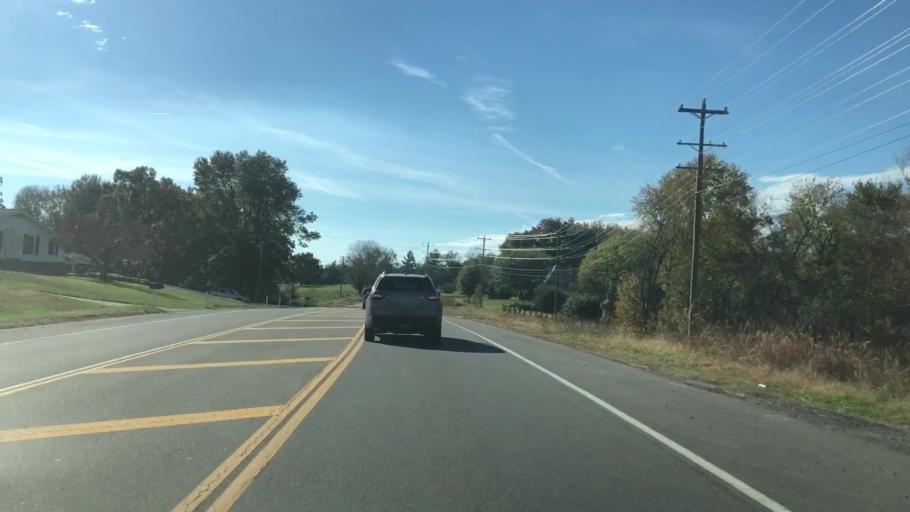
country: US
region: Virginia
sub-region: Prince William County
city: Gainesville
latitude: 38.7528
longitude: -77.6242
